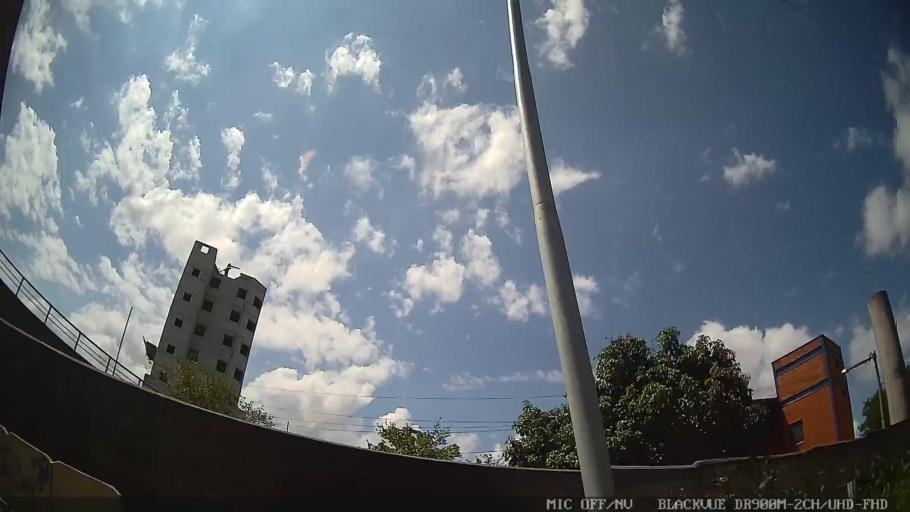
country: BR
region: Sao Paulo
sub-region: Guarulhos
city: Guarulhos
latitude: -23.5419
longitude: -46.4787
